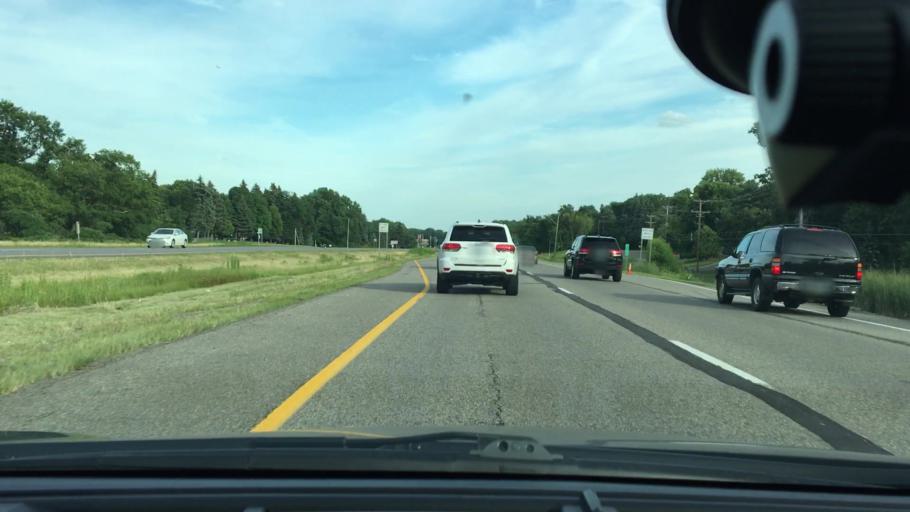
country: US
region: Minnesota
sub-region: Hennepin County
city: Plymouth
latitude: 44.9955
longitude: -93.4378
